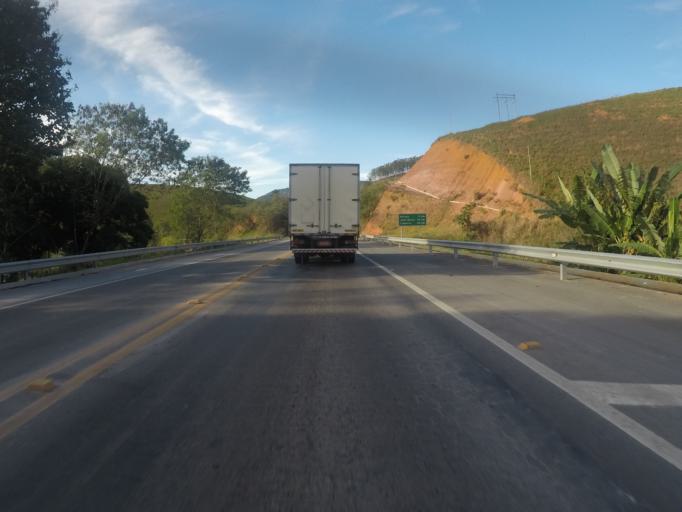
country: BR
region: Espirito Santo
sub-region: Ibiracu
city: Ibiracu
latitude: -19.8389
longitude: -40.3829
